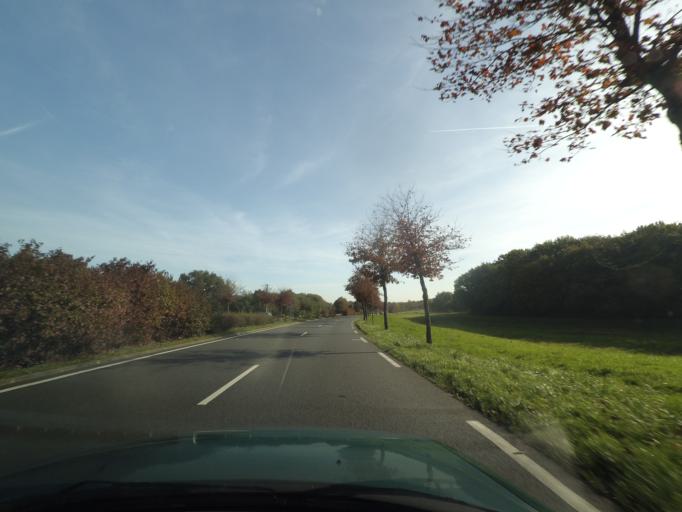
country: FR
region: Pays de la Loire
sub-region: Departement de Maine-et-Loire
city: Cholet
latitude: 47.0754
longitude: -0.8914
